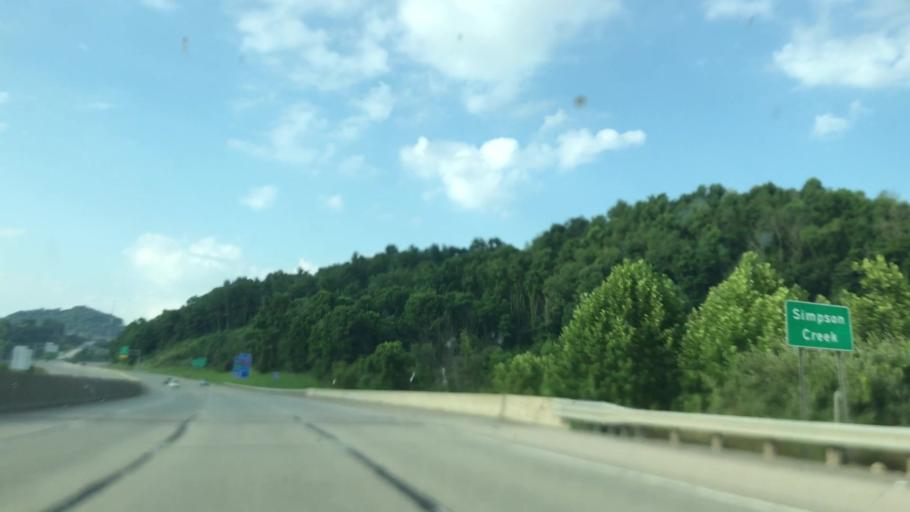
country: US
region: West Virginia
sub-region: Harrison County
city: Bridgeport
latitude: 39.2994
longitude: -80.2793
